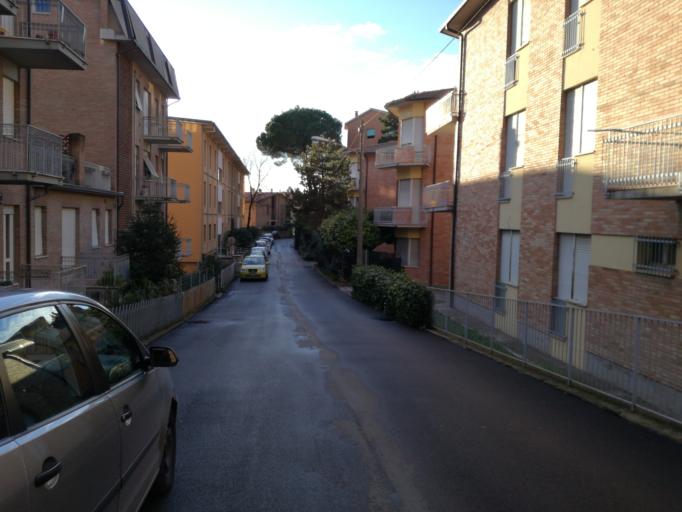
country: IT
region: Umbria
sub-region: Provincia di Perugia
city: Perugia
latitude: 43.1185
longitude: 12.3807
